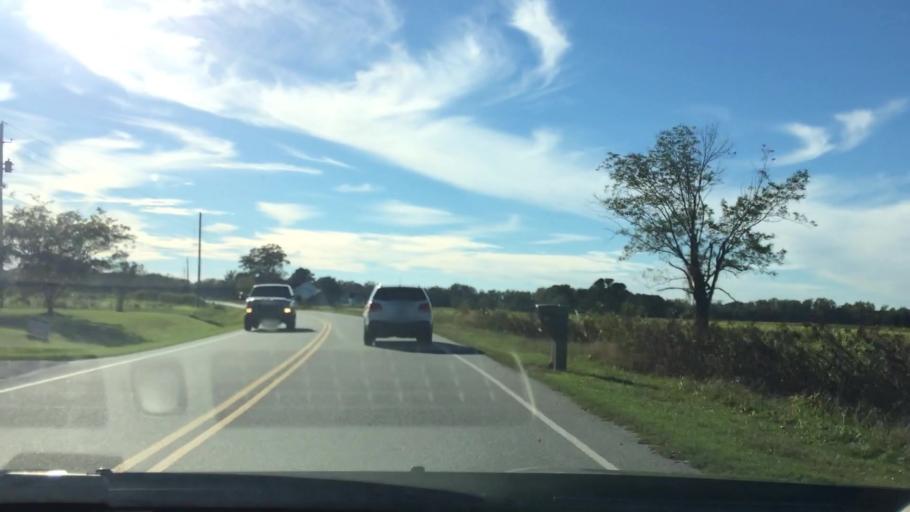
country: US
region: North Carolina
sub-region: Pitt County
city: Ayden
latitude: 35.4760
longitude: -77.4603
